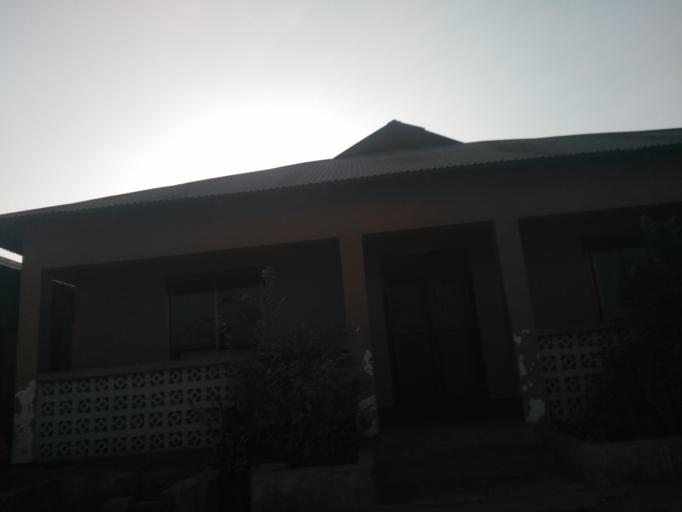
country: TZ
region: Dar es Salaam
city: Dar es Salaam
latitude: -6.9048
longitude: 39.2673
